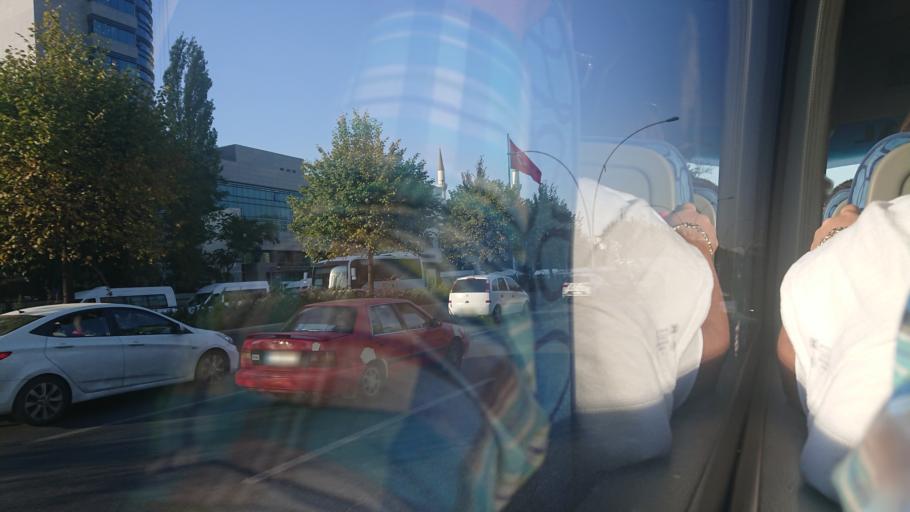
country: TR
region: Ankara
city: Ankara
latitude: 39.9388
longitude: 32.8254
